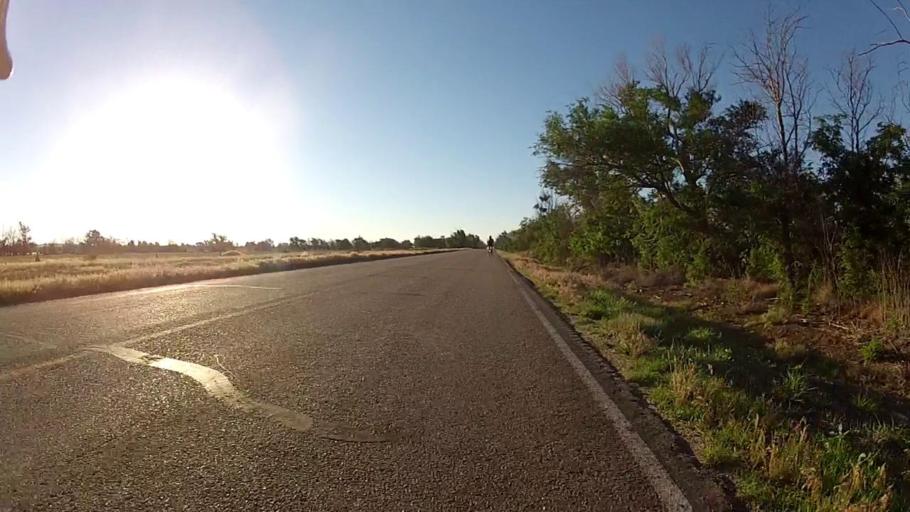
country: US
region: Kansas
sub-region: Ford County
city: Dodge City
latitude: 37.7147
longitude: -99.9315
